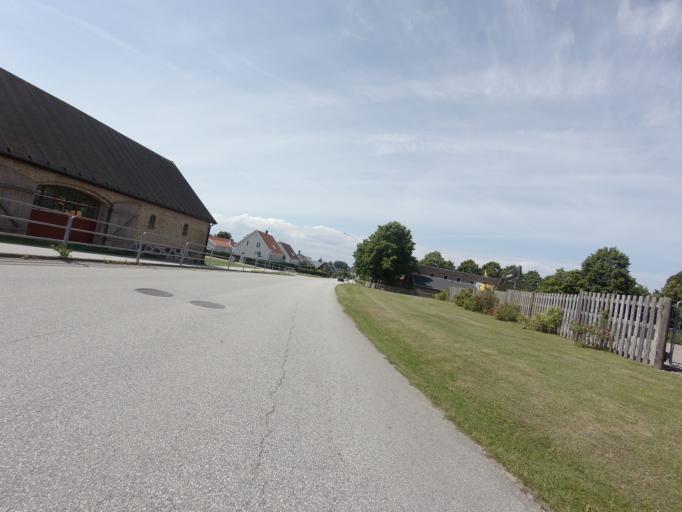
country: SE
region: Skane
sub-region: Helsingborg
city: Glumslov
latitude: 55.9410
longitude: 12.8103
